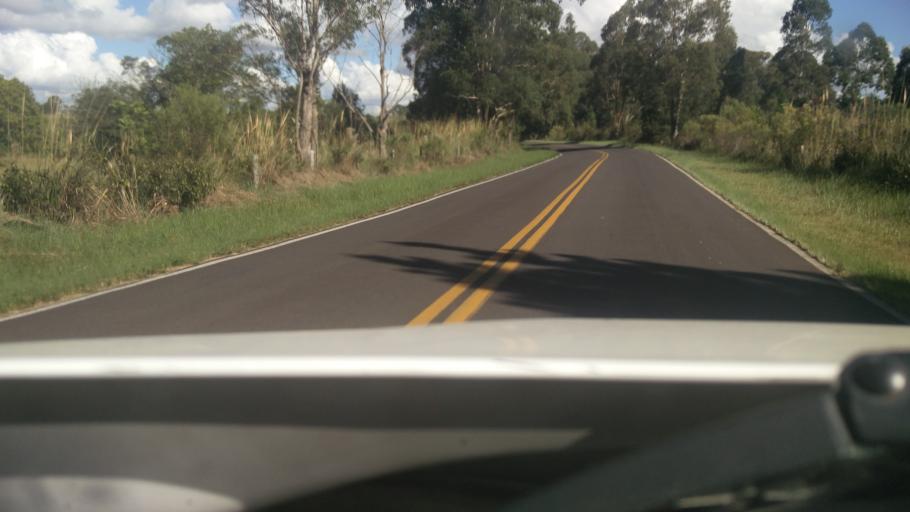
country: BR
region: Parana
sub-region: Palmeira
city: Palmeira
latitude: -25.4494
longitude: -49.8132
